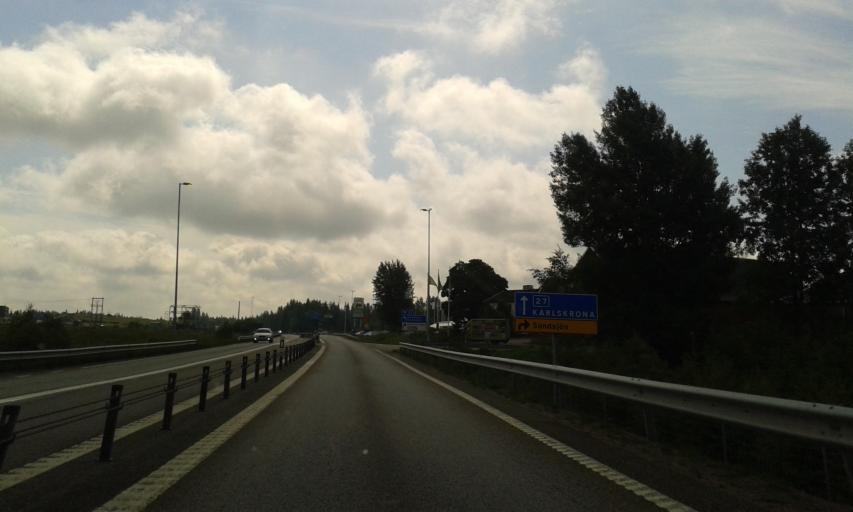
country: SE
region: Vaestra Goetaland
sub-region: Boras Kommun
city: Dalsjofors
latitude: 57.6179
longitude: 13.1091
